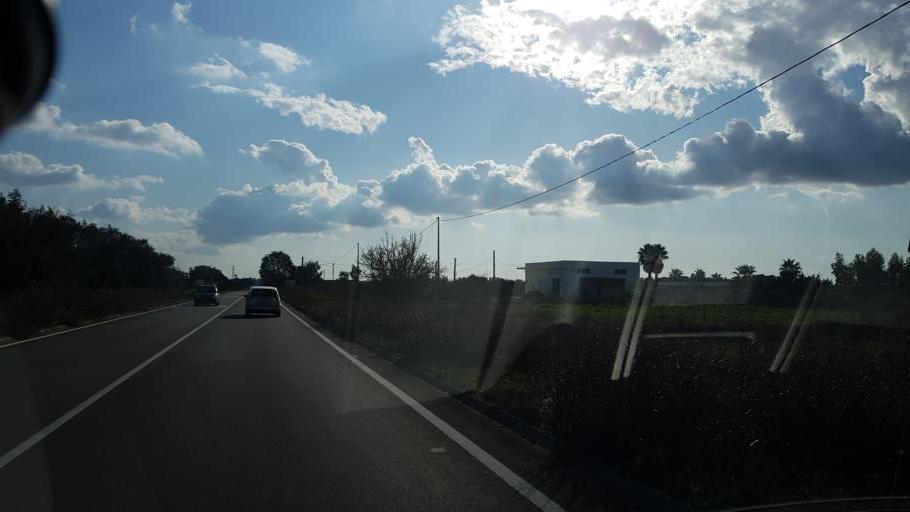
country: IT
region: Apulia
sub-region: Provincia di Lecce
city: Salice Salentino
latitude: 40.3626
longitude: 17.9676
